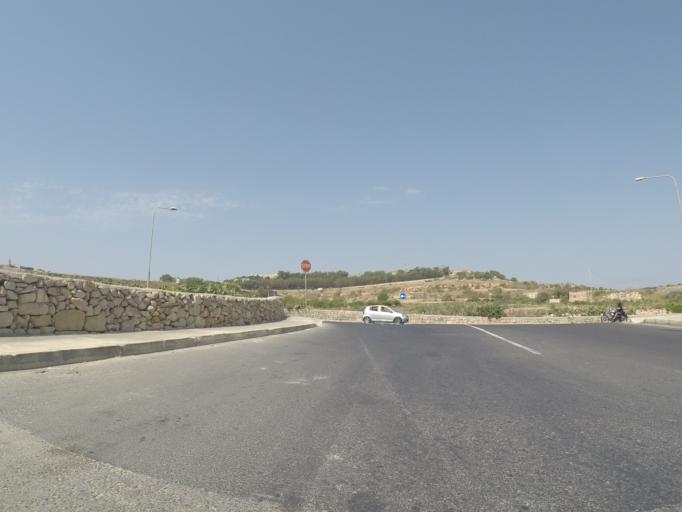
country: MT
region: L-Imdina
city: Imdina
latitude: 35.8946
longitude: 14.4101
